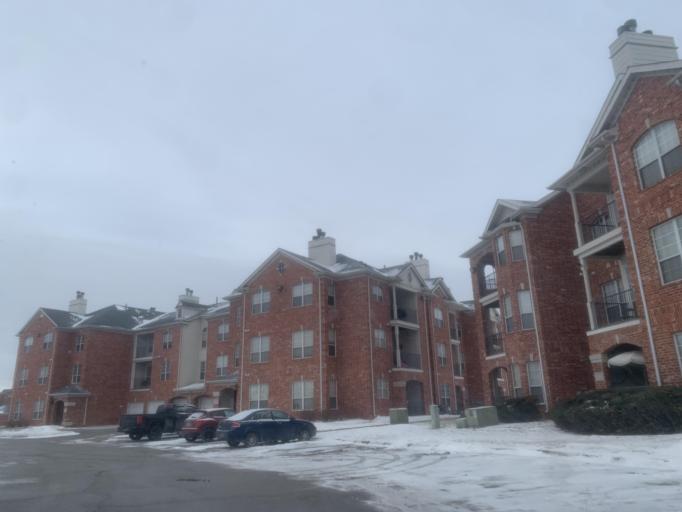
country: US
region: Nebraska
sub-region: Douglas County
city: Ralston
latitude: 41.2720
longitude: -96.0879
